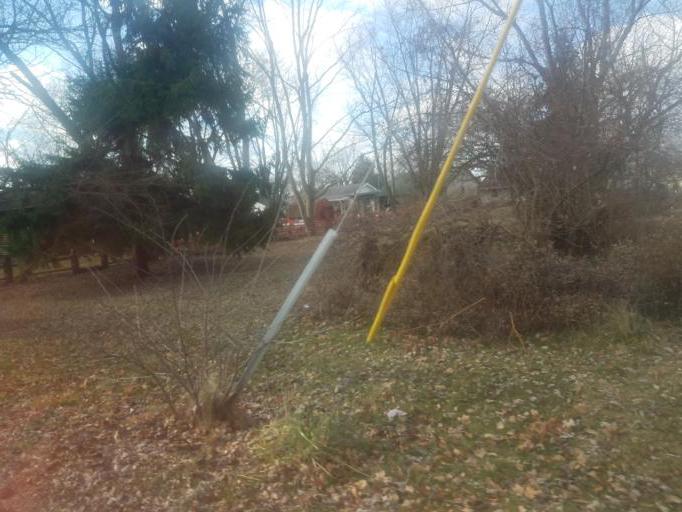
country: US
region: Ohio
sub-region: Marion County
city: Marion
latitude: 40.5835
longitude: -83.1551
